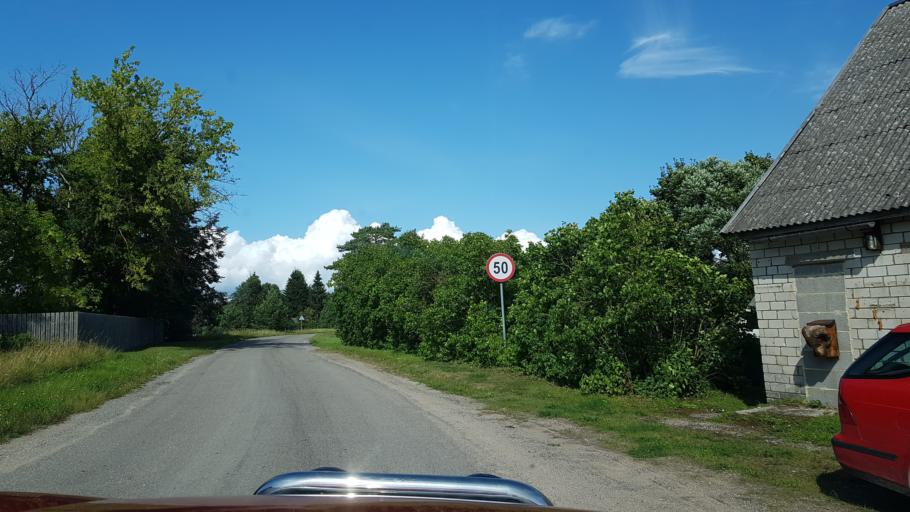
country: EE
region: Laeaene
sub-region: Lihula vald
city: Lihula
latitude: 58.4512
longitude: 23.7456
